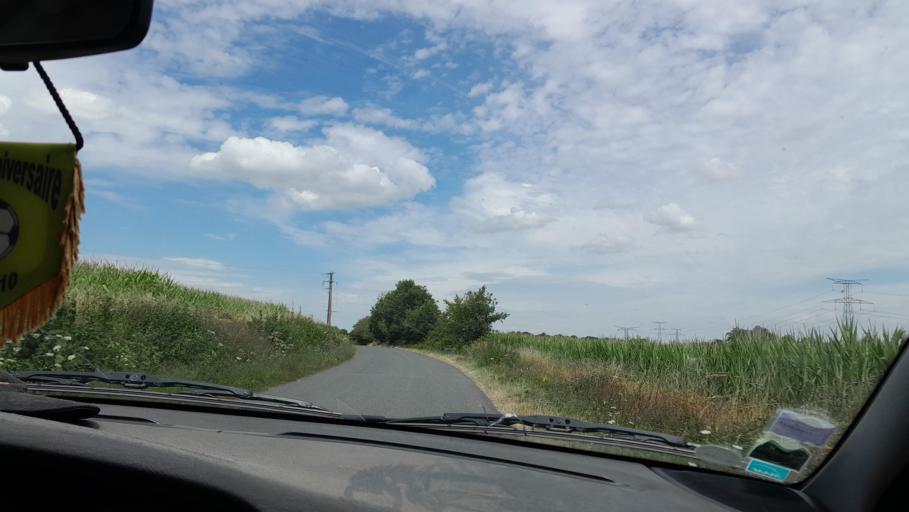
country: FR
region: Pays de la Loire
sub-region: Departement de la Mayenne
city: Saint-Pierre-la-Cour
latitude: 48.1586
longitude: -1.0312
